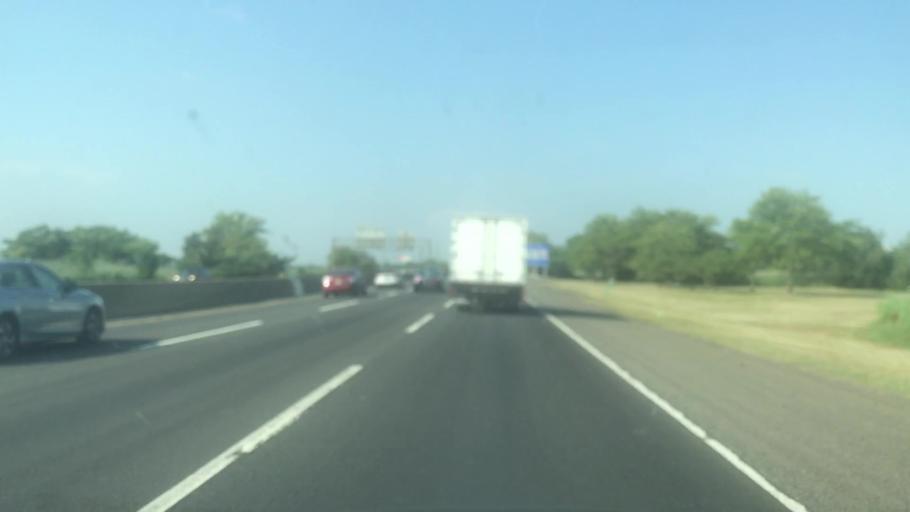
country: US
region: New Jersey
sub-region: Hudson County
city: North Bergen
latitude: 40.8015
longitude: -74.0357
